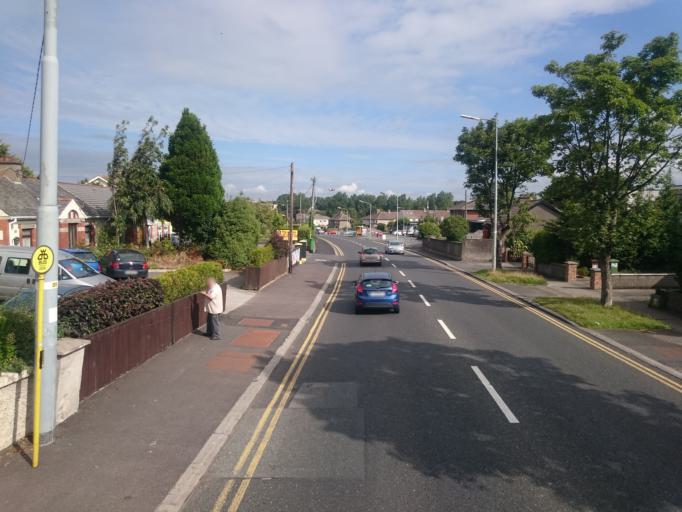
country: IE
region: Leinster
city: Oldbawn
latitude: 53.2830
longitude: -6.3595
